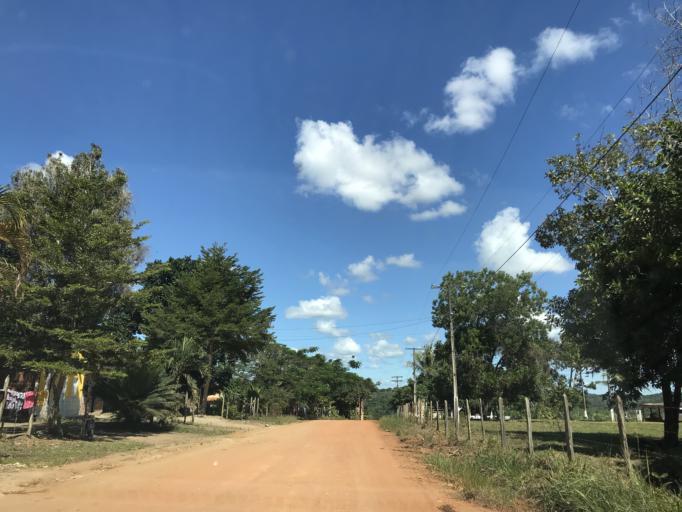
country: BR
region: Bahia
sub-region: Valenca
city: Valenca
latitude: -13.3202
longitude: -39.2402
